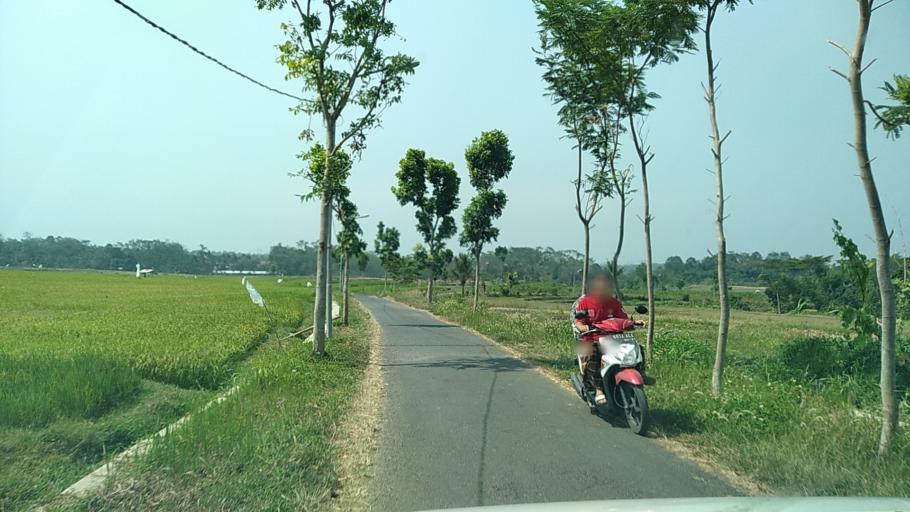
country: ID
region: Central Java
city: Ungaran
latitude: -7.0914
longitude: 110.3368
